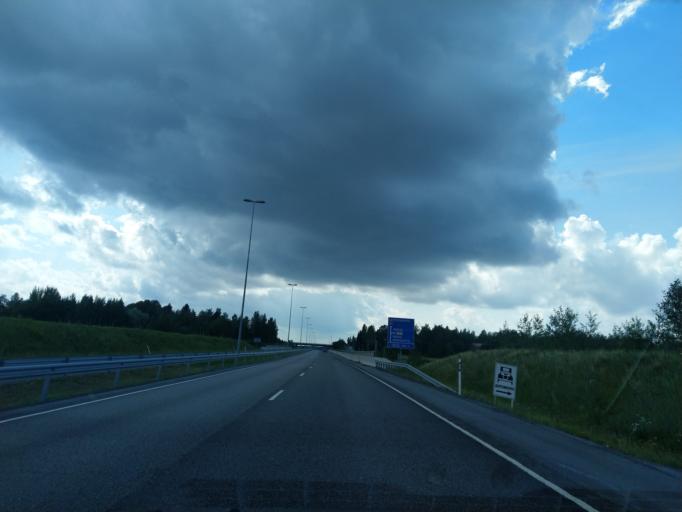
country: FI
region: South Karelia
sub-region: Imatra
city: Imatra
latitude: 61.1759
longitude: 28.7087
